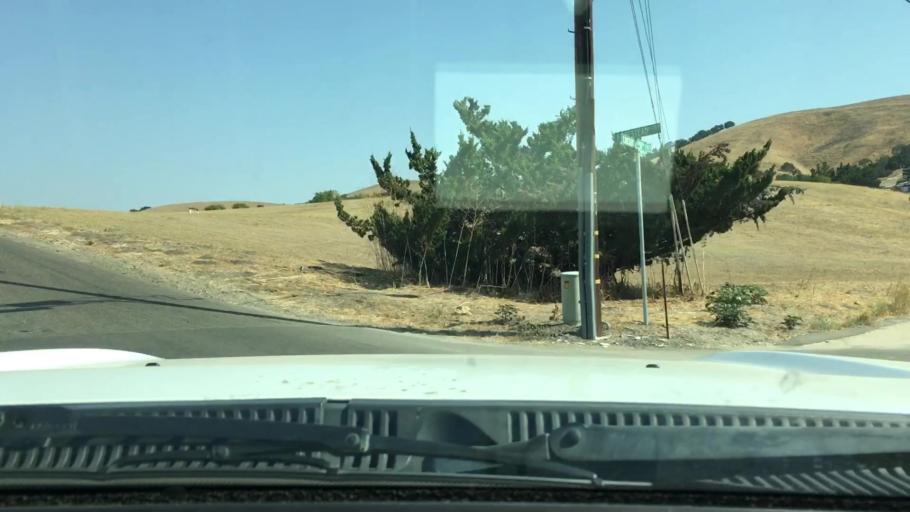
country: US
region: California
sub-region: San Luis Obispo County
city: Atascadero
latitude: 35.5107
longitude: -120.6381
